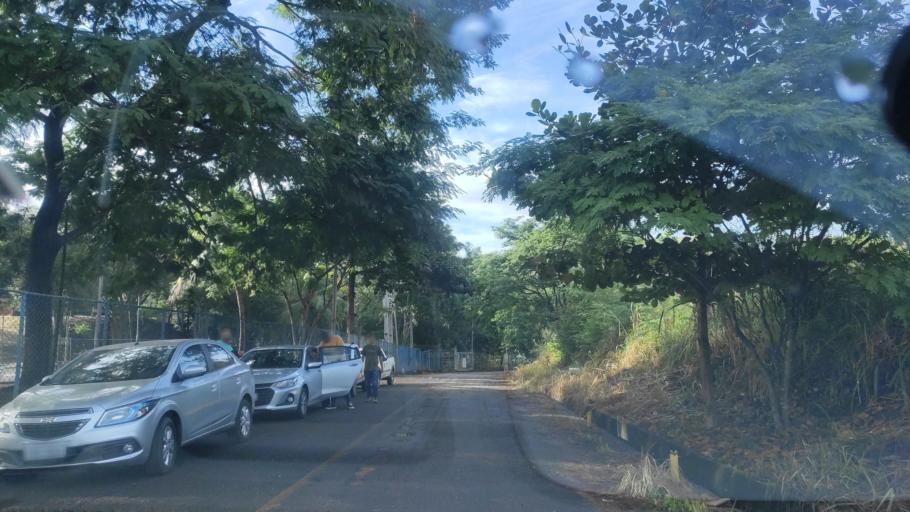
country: BR
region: Espirito Santo
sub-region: Nova Venecia
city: Nova Venecia
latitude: -18.7142
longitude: -40.3775
